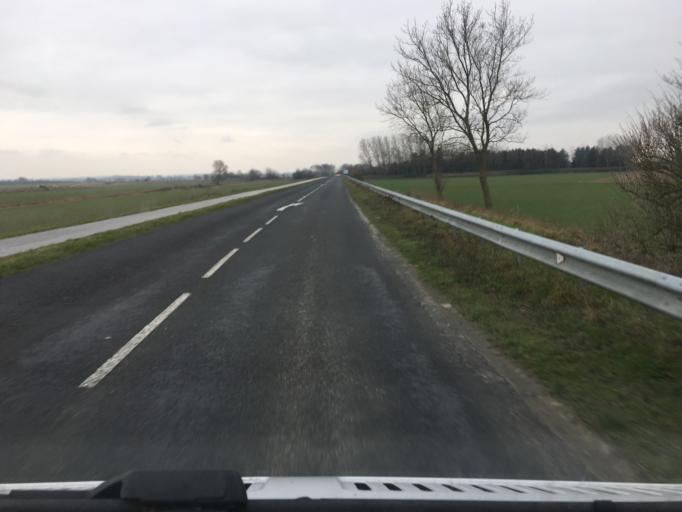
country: FR
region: Picardie
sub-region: Departement de la Somme
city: Pende
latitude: 50.2047
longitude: 1.5571
